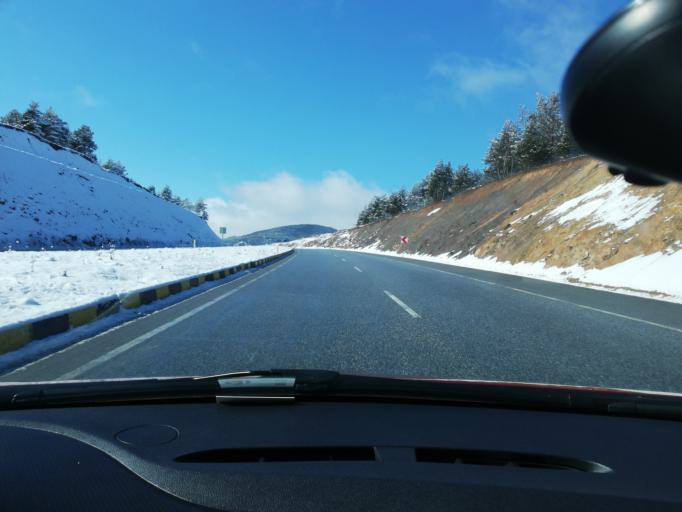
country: TR
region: Kastamonu
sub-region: Cide
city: Kastamonu
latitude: 41.3534
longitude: 33.6592
